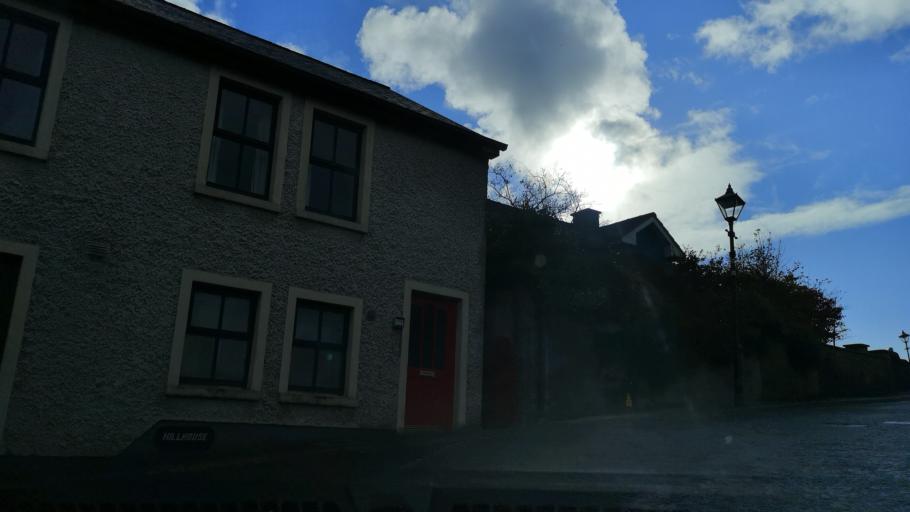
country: IE
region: Connaught
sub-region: Maigh Eo
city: Westport
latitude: 53.7971
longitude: -9.5226
